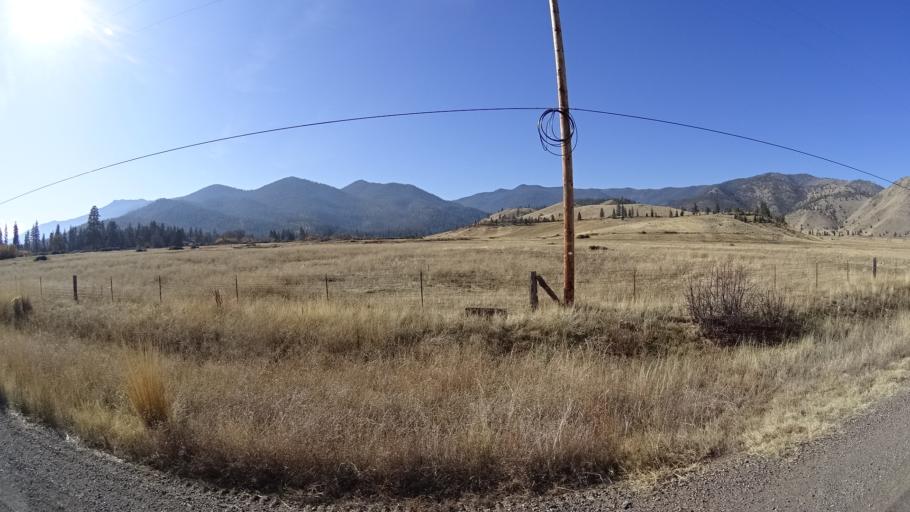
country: US
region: California
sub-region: Siskiyou County
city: Weed
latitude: 41.4507
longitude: -122.4541
